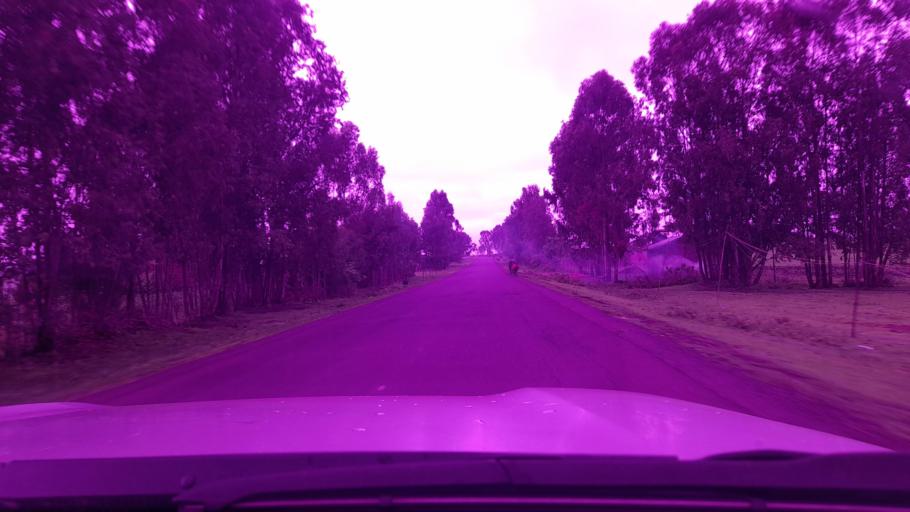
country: ET
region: Oromiya
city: Waliso
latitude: 8.2743
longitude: 37.6691
